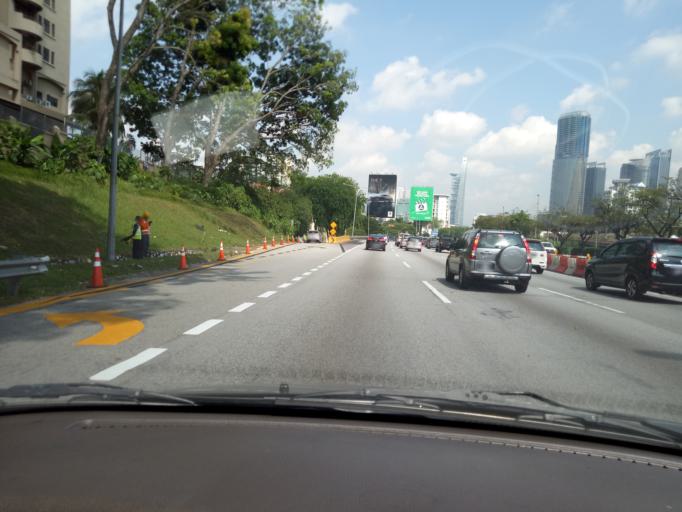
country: MY
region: Kuala Lumpur
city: Kuala Lumpur
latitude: 3.1121
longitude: 101.6852
